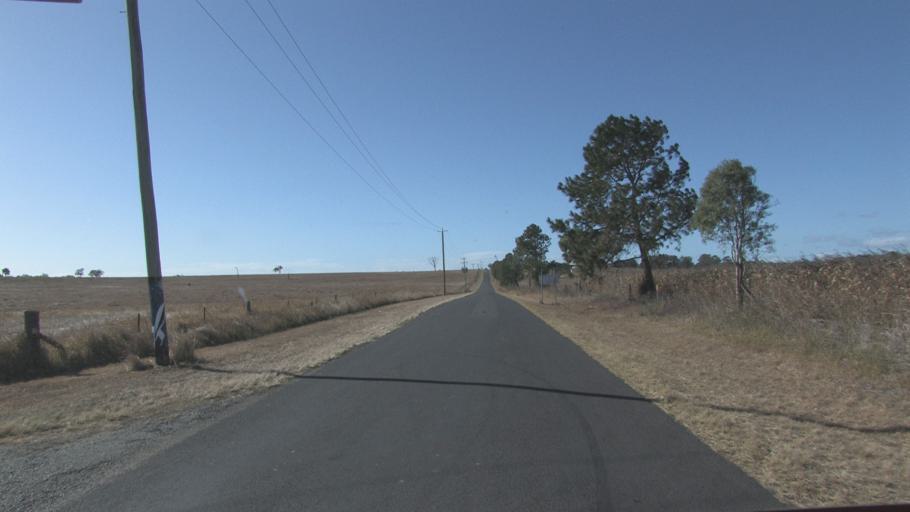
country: AU
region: Queensland
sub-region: Logan
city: Cedar Vale
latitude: -27.8532
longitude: 152.9626
